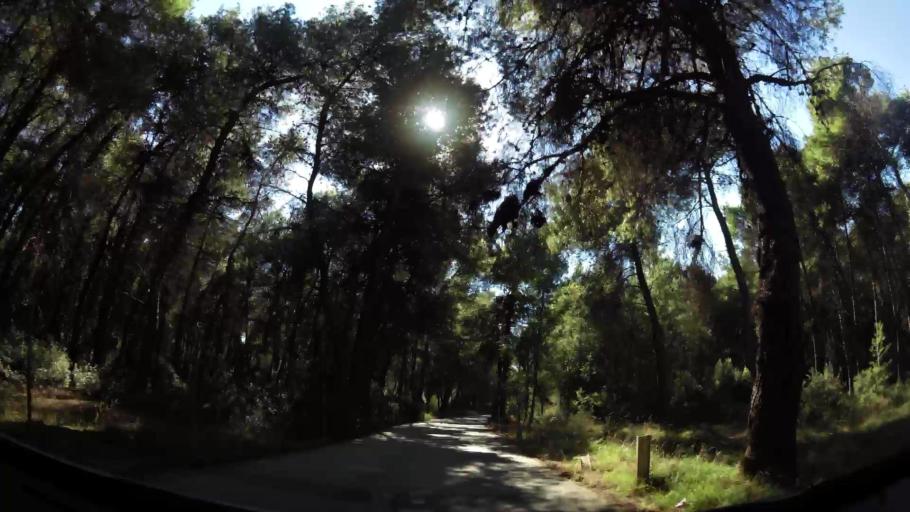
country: GR
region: Attica
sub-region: Nomarchia Athinas
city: Ekali
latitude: 38.1115
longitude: 23.8264
